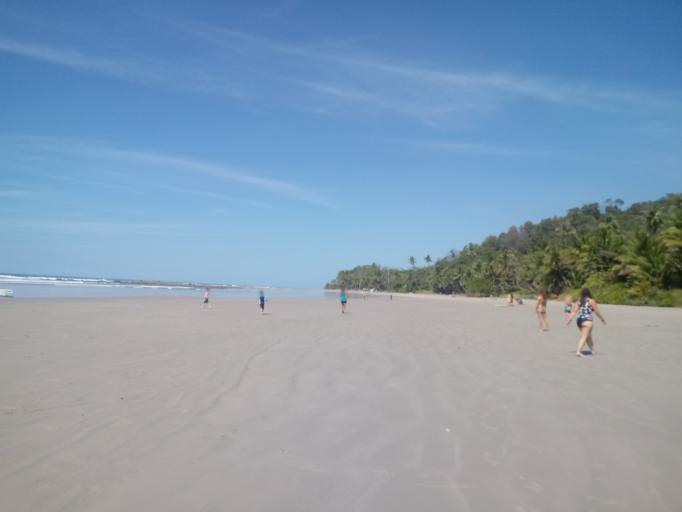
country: CR
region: Guanacaste
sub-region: Canton de Nandayure
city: Bejuco
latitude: 9.6661
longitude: -85.1949
